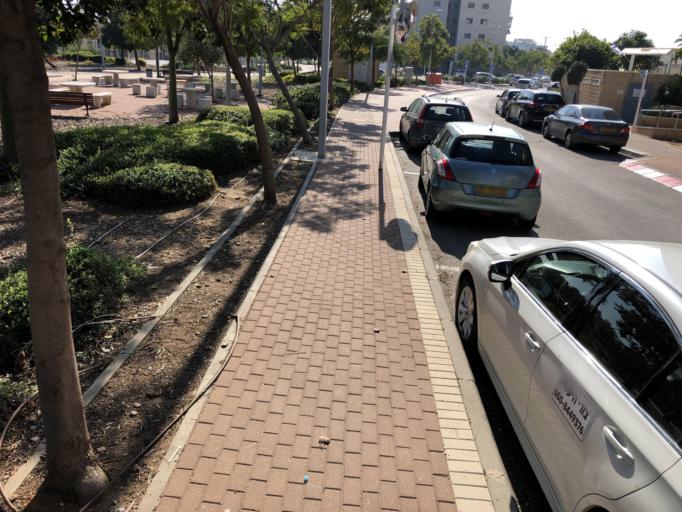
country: IL
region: Northern District
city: `Akko
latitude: 32.9312
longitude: 35.0963
